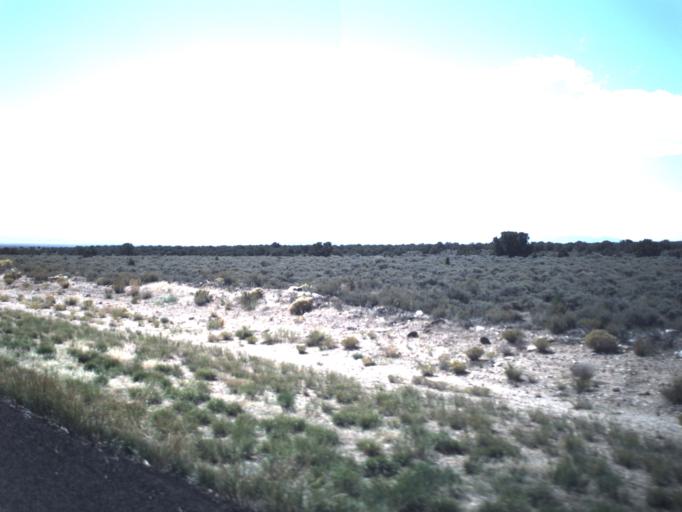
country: US
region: Utah
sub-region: Iron County
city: Parowan
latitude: 38.0256
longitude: -112.9982
